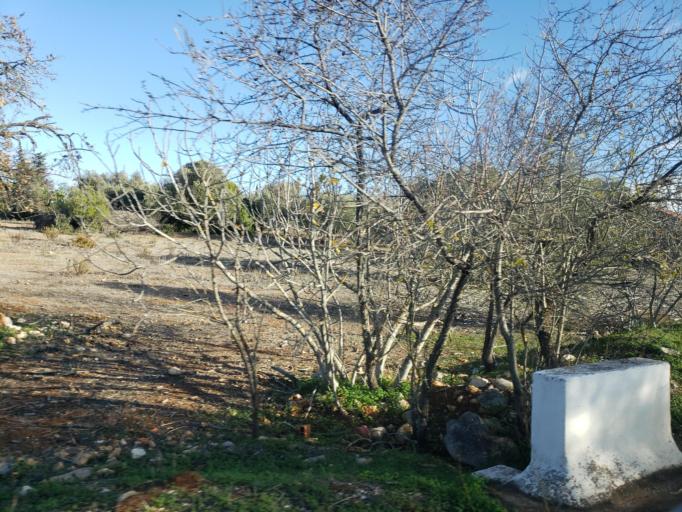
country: PT
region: Faro
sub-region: Portimao
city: Alvor
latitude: 37.1876
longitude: -8.5873
